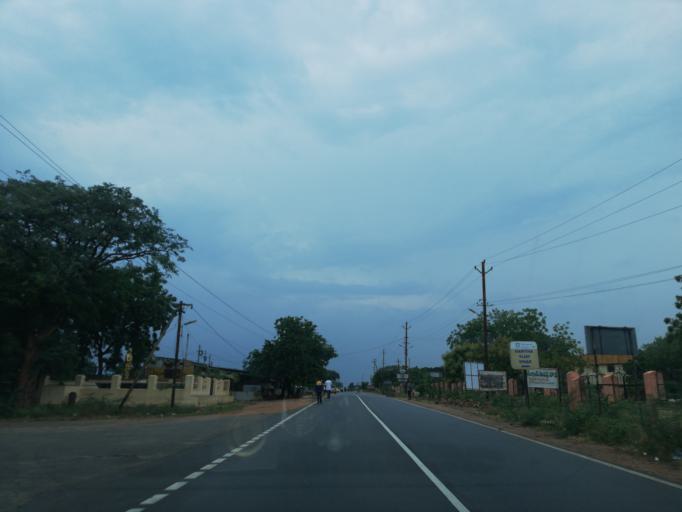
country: IN
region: Andhra Pradesh
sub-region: Guntur
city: Macherla
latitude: 16.6121
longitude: 79.2979
